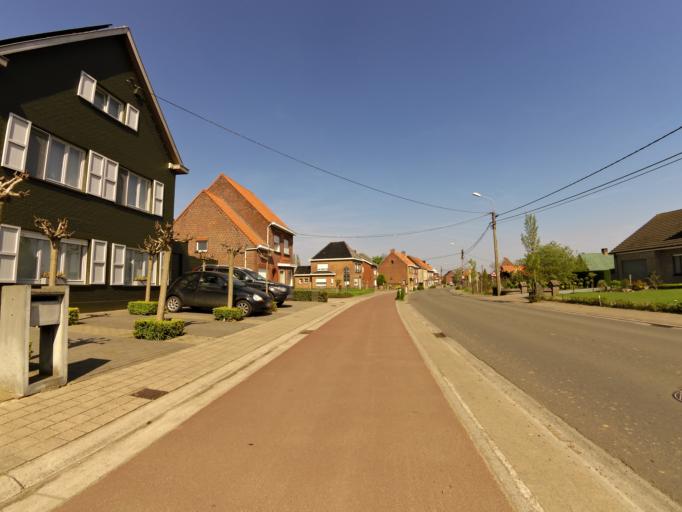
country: BE
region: Flanders
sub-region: Provincie West-Vlaanderen
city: Torhout
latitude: 51.0588
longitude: 3.0906
